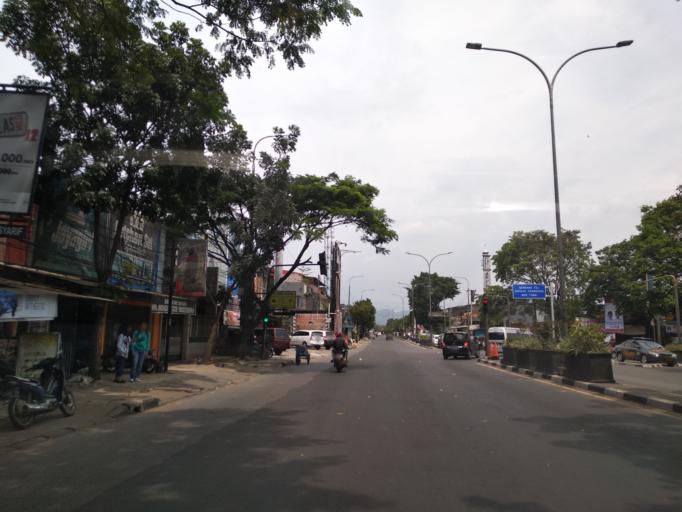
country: ID
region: West Java
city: Bandung
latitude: -6.9616
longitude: 107.6388
